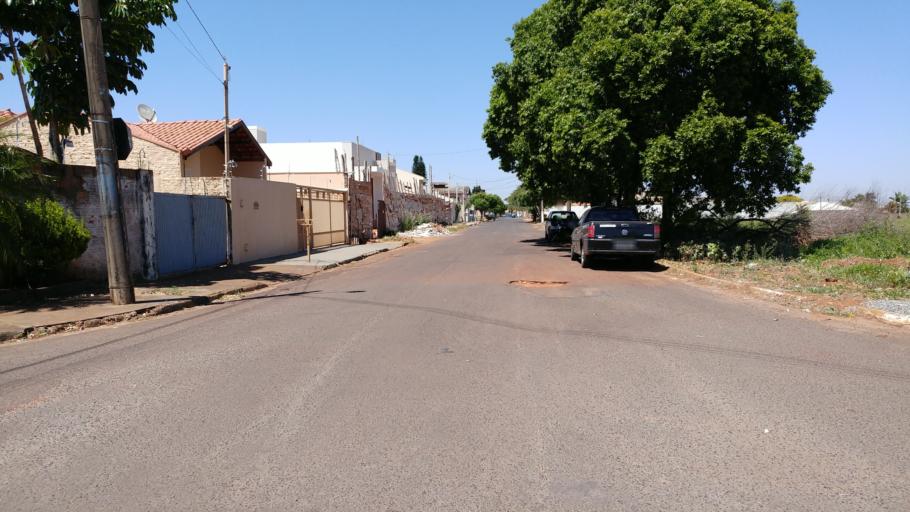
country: BR
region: Sao Paulo
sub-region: Paraguacu Paulista
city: Paraguacu Paulista
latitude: -22.4086
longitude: -50.5831
